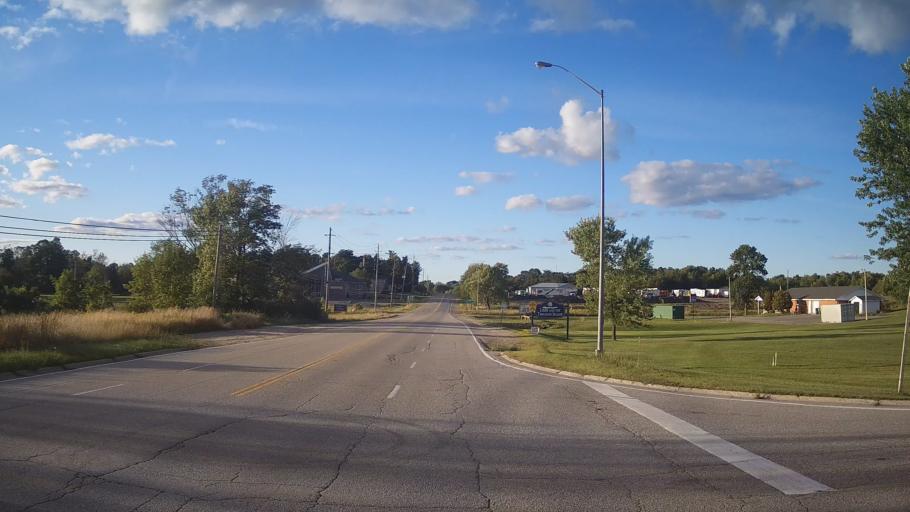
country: CA
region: Ontario
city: Gananoque
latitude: 44.3465
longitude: -76.1713
